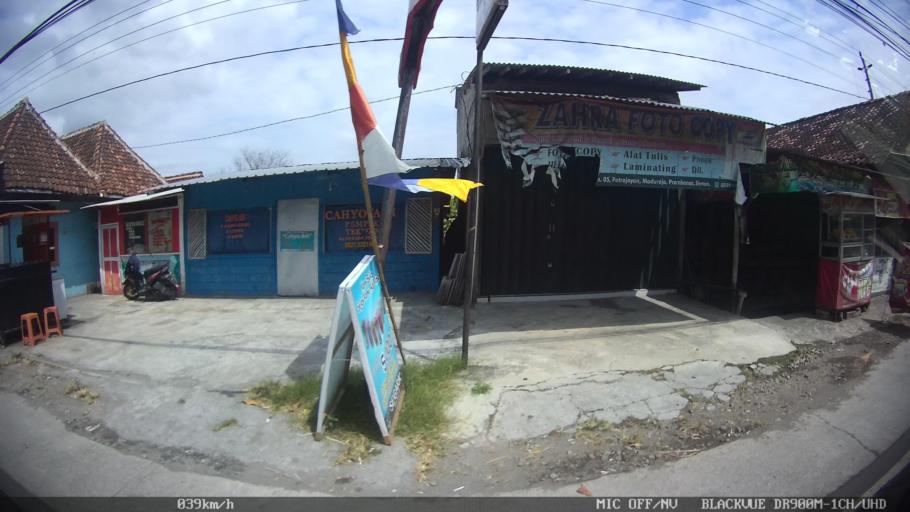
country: ID
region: Central Java
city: Candi Prambanan
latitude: -7.7923
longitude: 110.4827
